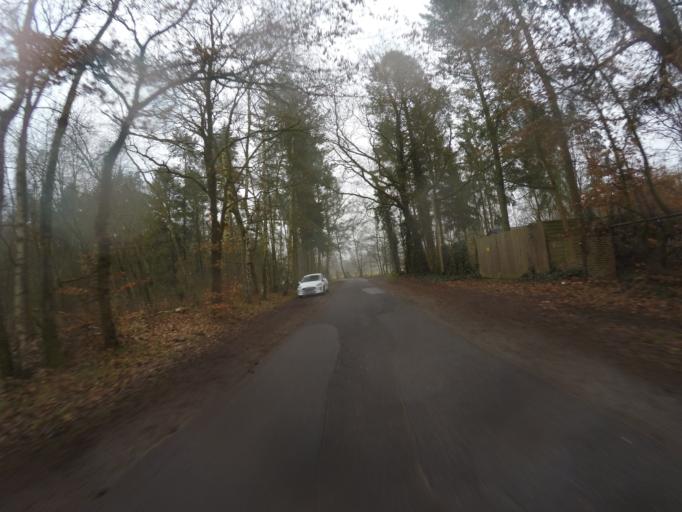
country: DE
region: Schleswig-Holstein
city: Quickborn
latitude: 53.7202
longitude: 9.9312
